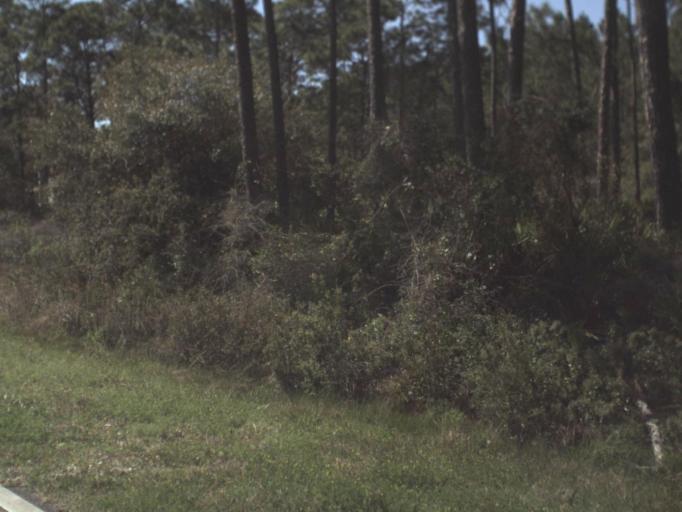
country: US
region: Florida
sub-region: Franklin County
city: Carrabelle
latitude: 29.9082
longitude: -84.5402
